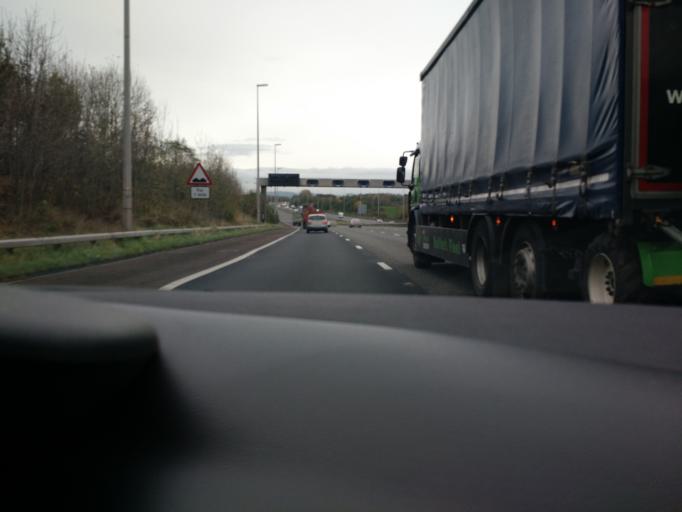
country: GB
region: England
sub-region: Lancashire
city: Goosnargh
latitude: 53.7952
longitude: -2.6770
